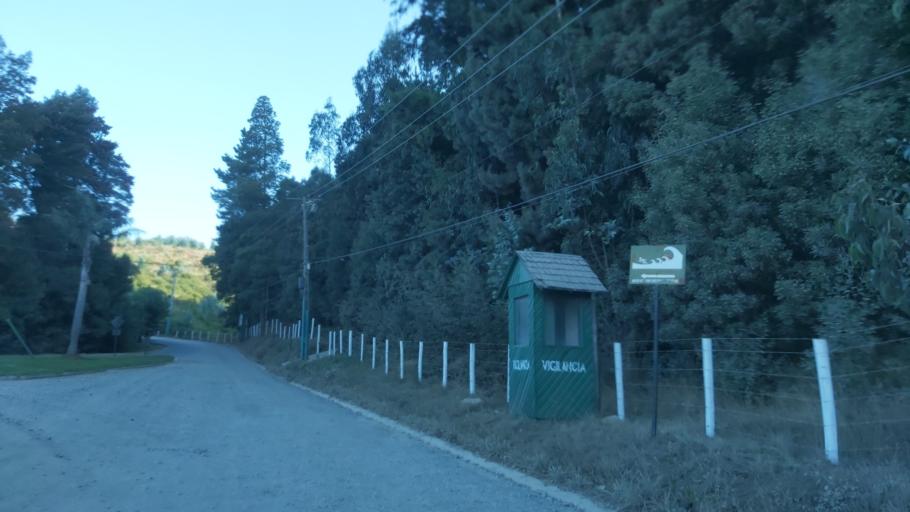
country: CL
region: Biobio
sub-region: Provincia de Concepcion
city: Tome
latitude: -36.5343
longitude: -72.9309
